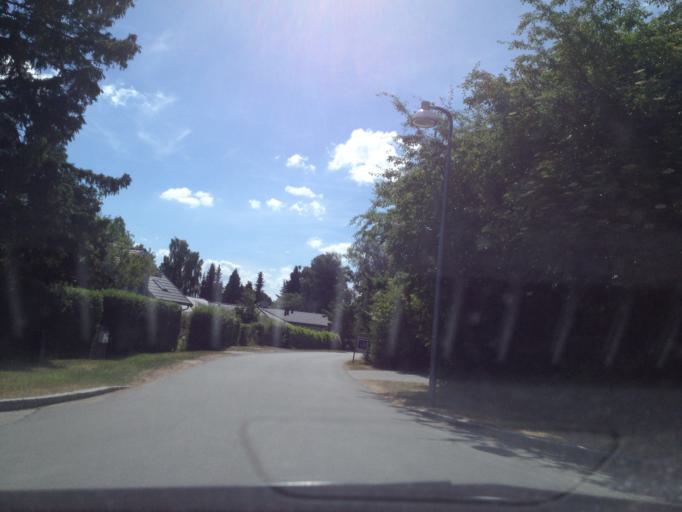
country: DK
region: Capital Region
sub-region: Horsholm Kommune
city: Horsholm
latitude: 55.8613
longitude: 12.5050
